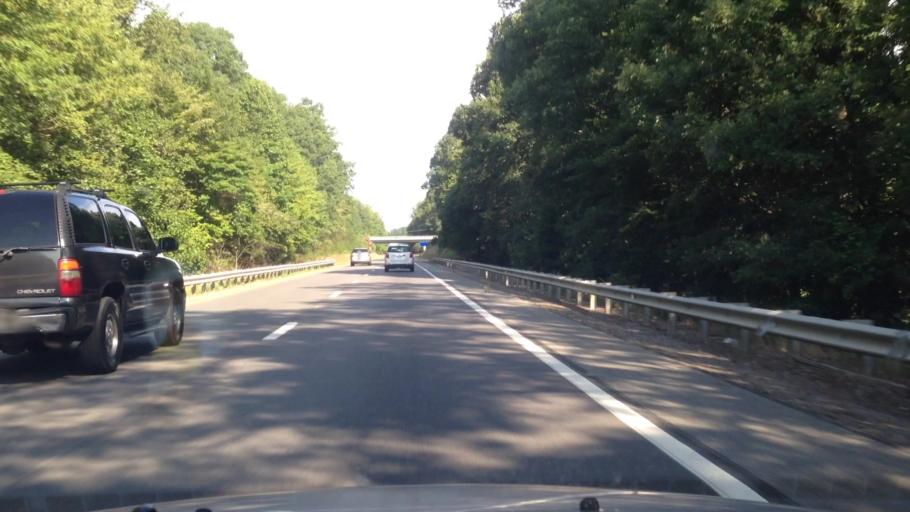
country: US
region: Virginia
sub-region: Henry County
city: Horse Pasture
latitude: 36.6408
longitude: -79.8964
